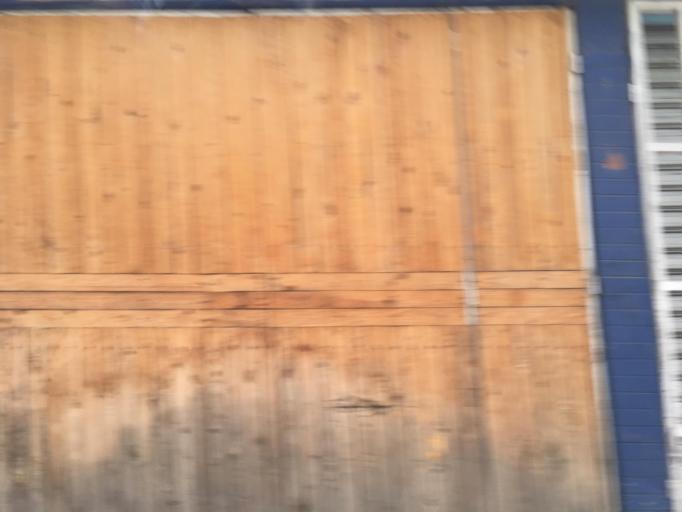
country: GT
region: Guatemala
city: Villa Canales
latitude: 14.4389
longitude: -90.5581
